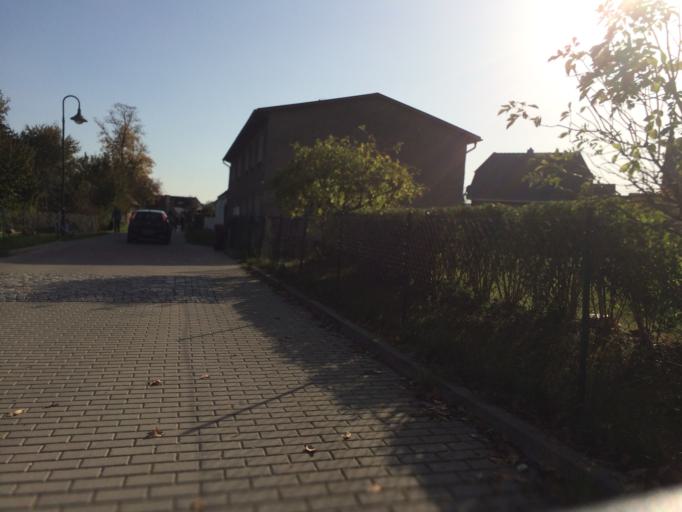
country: DE
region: Berlin
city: Blankenfelde
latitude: 52.6652
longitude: 13.3752
